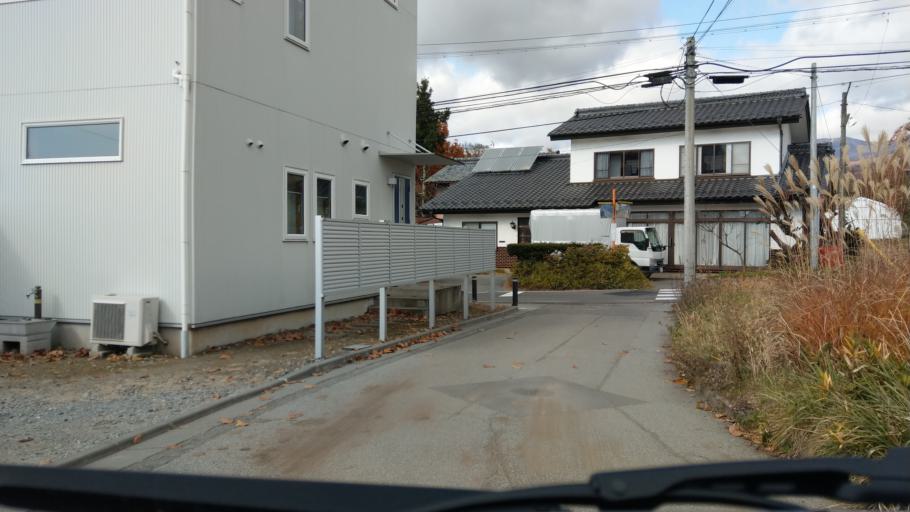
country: JP
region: Nagano
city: Komoro
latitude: 36.3223
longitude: 138.4952
